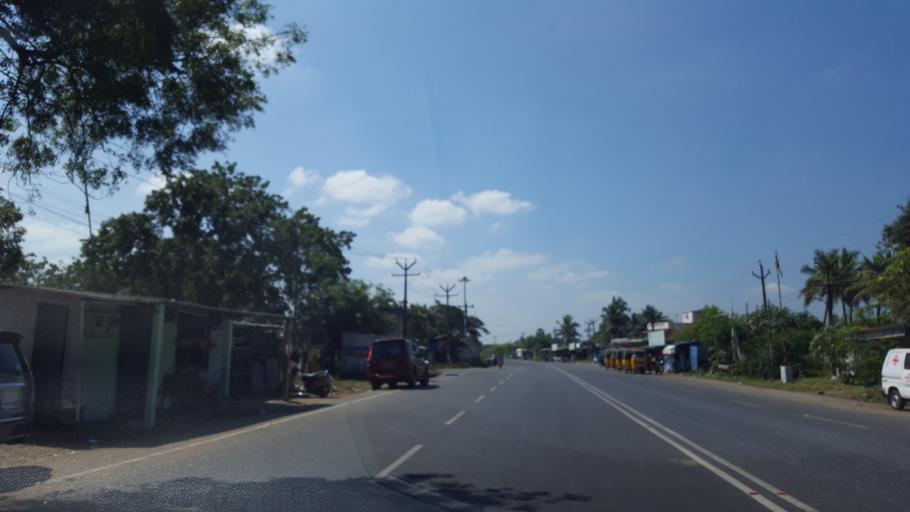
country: IN
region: Tamil Nadu
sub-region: Kancheepuram
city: Mamallapuram
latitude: 12.6949
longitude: 80.1814
